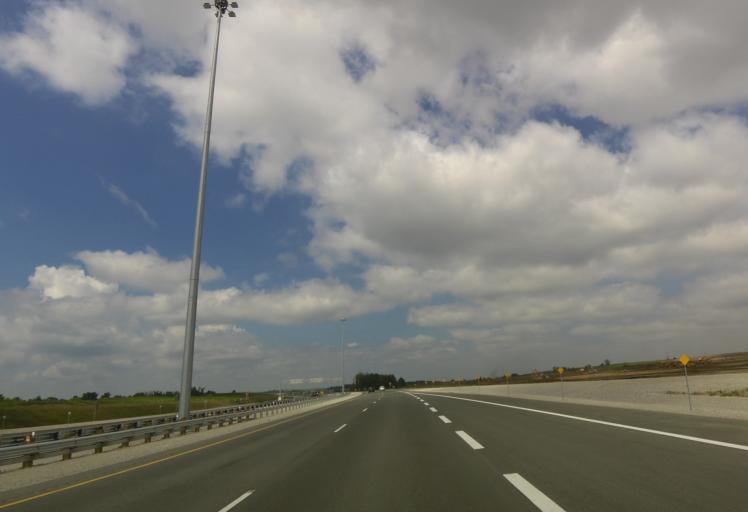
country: CA
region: Ontario
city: Ajax
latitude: 43.8744
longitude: -78.9771
